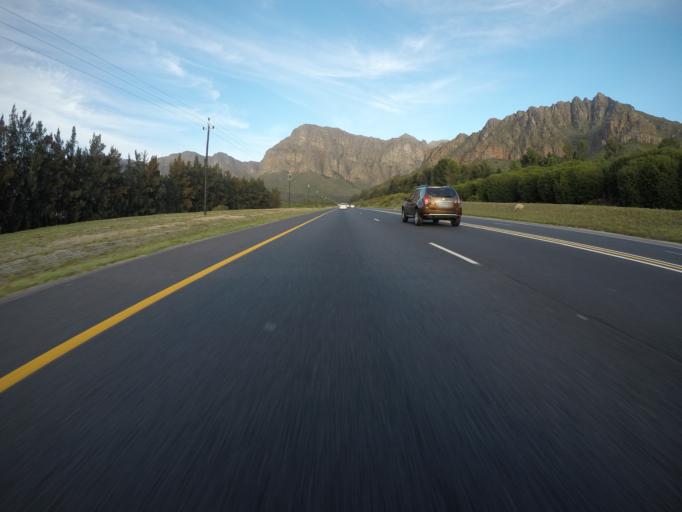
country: ZA
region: Western Cape
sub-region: Cape Winelands District Municipality
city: Paarl
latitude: -33.7436
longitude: 19.0468
